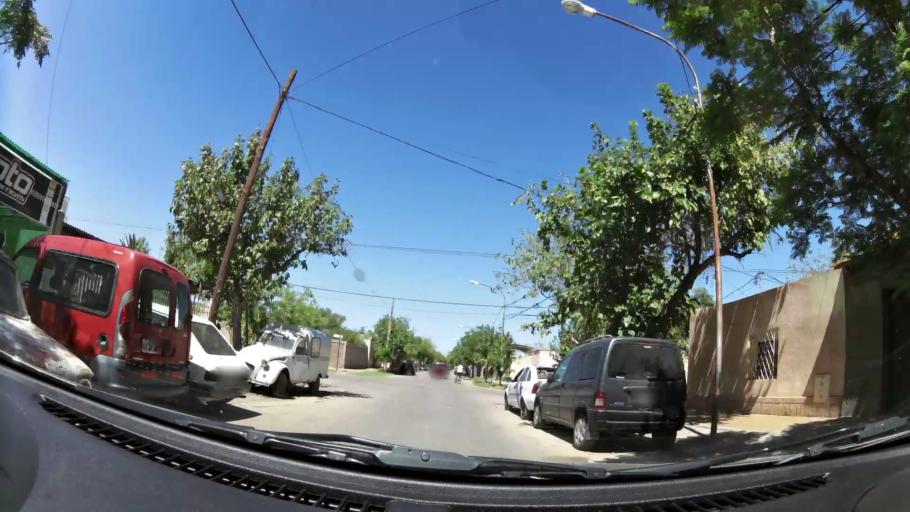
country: AR
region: San Juan
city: San Juan
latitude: -31.5179
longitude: -68.5205
